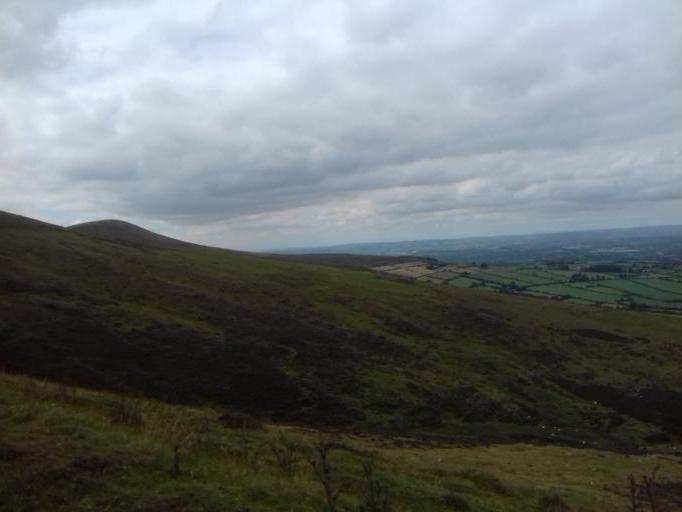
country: IE
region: Leinster
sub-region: Loch Garman
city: Bunclody
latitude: 52.6391
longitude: -6.7773
